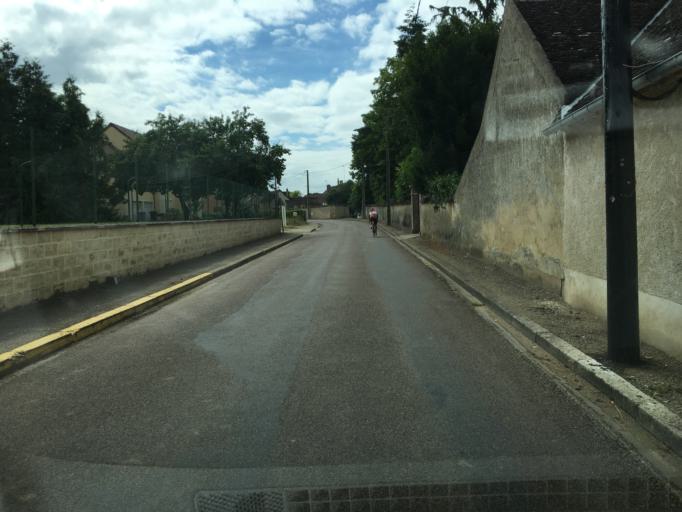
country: FR
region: Bourgogne
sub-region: Departement de l'Yonne
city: Joigny
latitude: 47.9524
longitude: 3.4346
